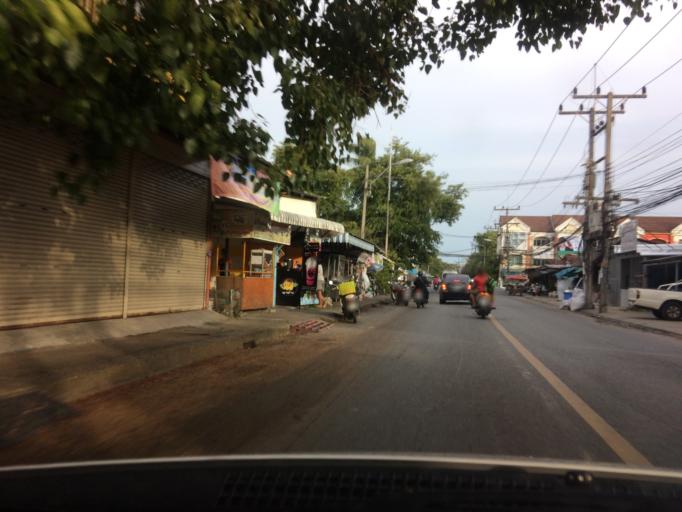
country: TH
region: Phuket
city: Ban Talat Yai
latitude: 7.8825
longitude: 98.4026
